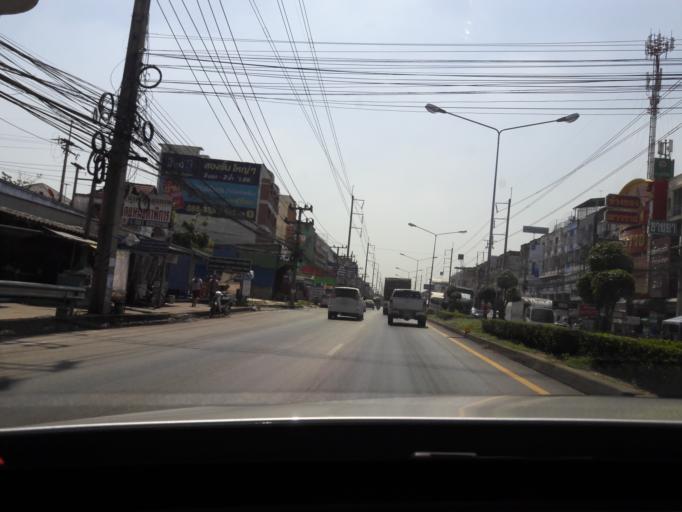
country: TH
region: Samut Sakhon
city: Krathum Baen
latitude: 13.6242
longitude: 100.2927
